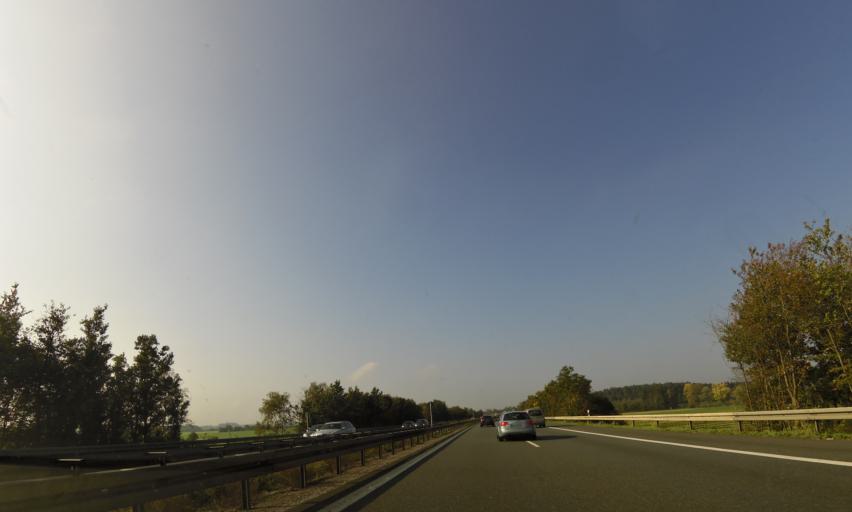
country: DE
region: Bavaria
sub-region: Regierungsbezirk Mittelfranken
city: Dombuhl
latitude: 49.2318
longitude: 10.3103
